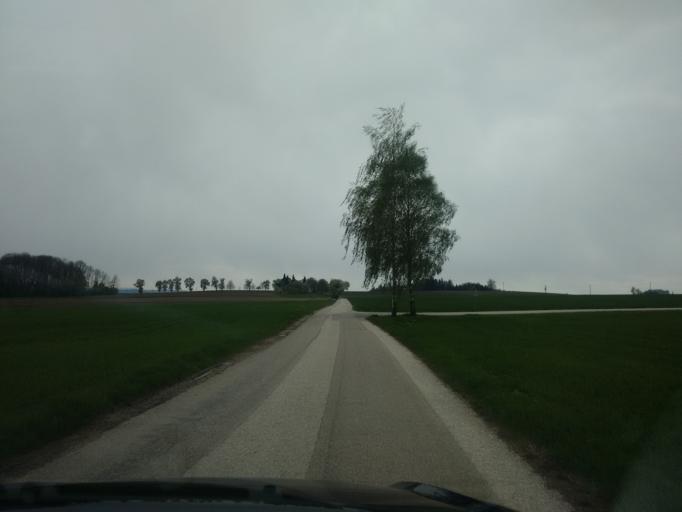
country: AT
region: Upper Austria
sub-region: Wels-Land
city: Buchkirchen
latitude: 48.2101
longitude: 14.0221
